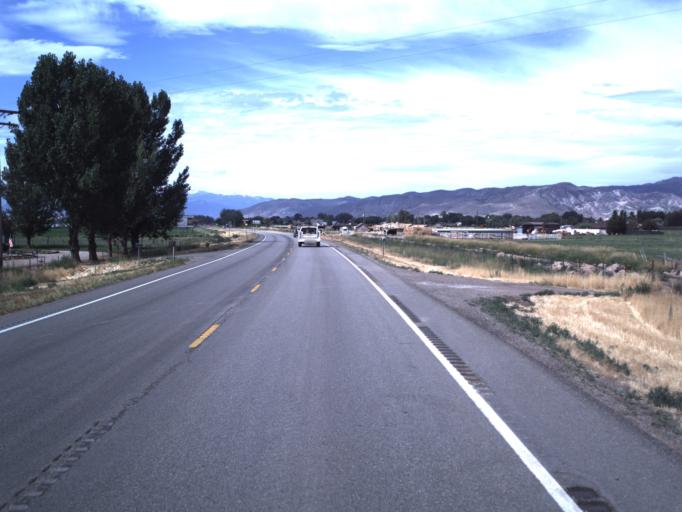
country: US
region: Utah
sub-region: Sevier County
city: Richfield
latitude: 38.7829
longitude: -112.0584
